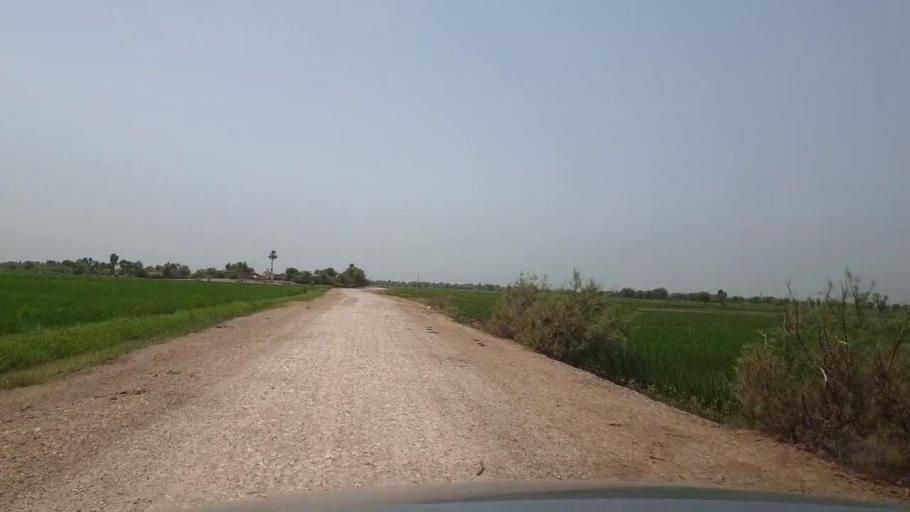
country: PK
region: Sindh
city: Madeji
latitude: 27.7776
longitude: 68.4073
